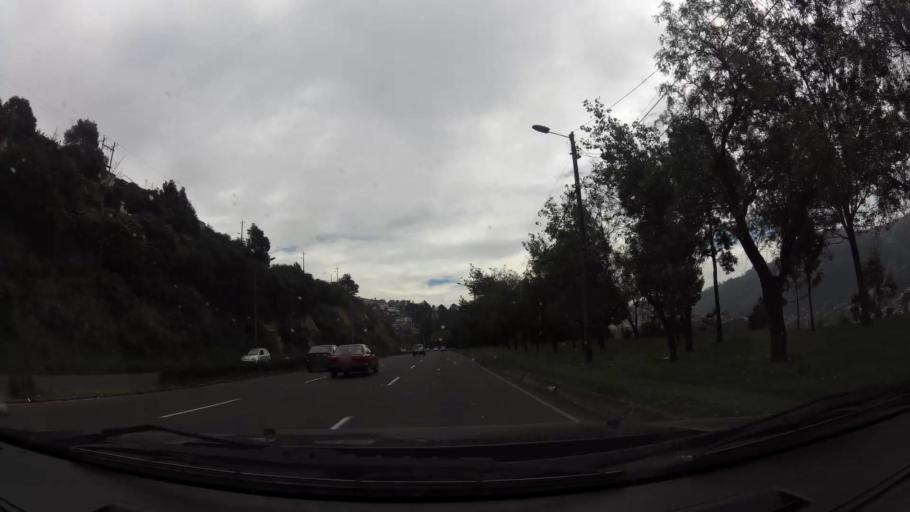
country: EC
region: Pichincha
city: Quito
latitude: -0.2237
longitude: -78.4963
